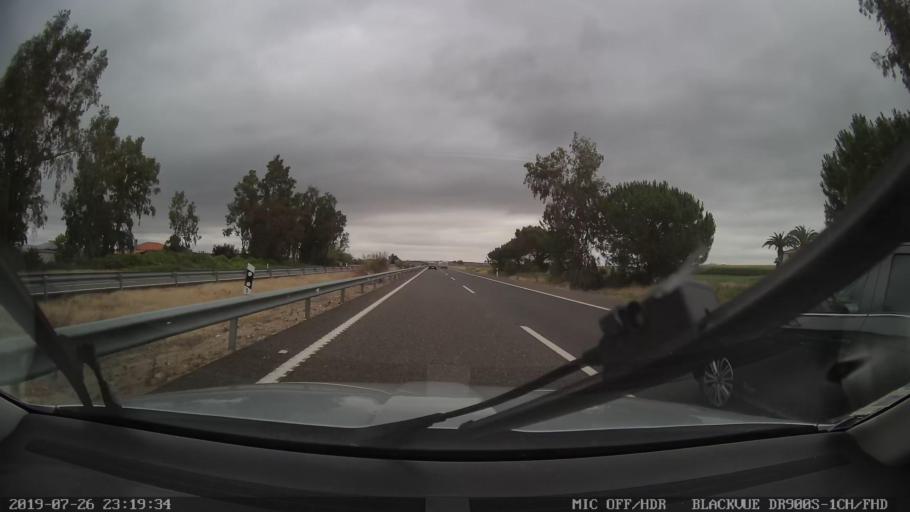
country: ES
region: Extremadura
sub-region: Provincia de Caceres
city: Almoharin
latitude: 39.1089
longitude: -5.9891
